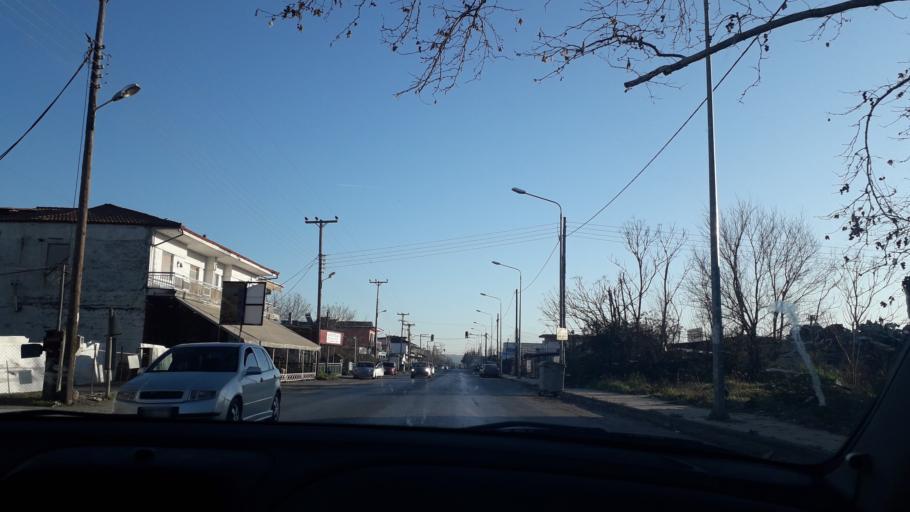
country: GR
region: Central Macedonia
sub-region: Nomos Imathias
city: Alexandreia
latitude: 40.6205
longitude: 22.4474
